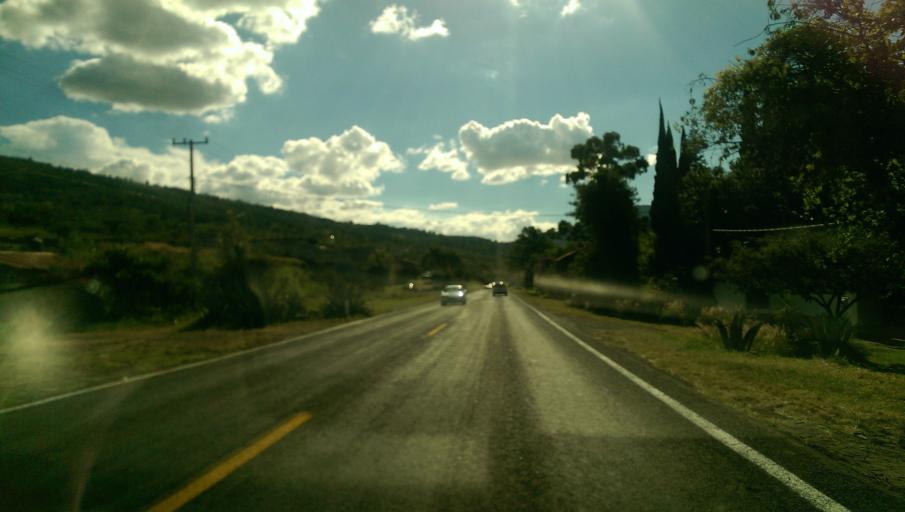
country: MX
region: Michoacan
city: Tzintzuntzan
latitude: 19.6373
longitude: -101.5512
